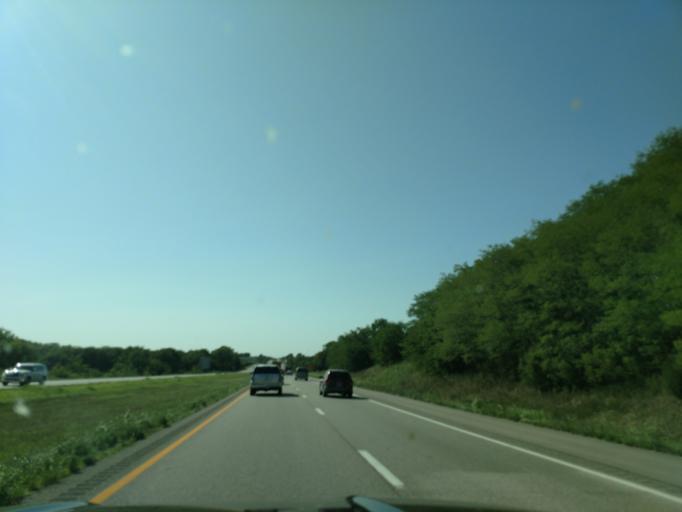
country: US
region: Missouri
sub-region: Andrew County
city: Country Club Village
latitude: 39.8666
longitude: -94.8242
